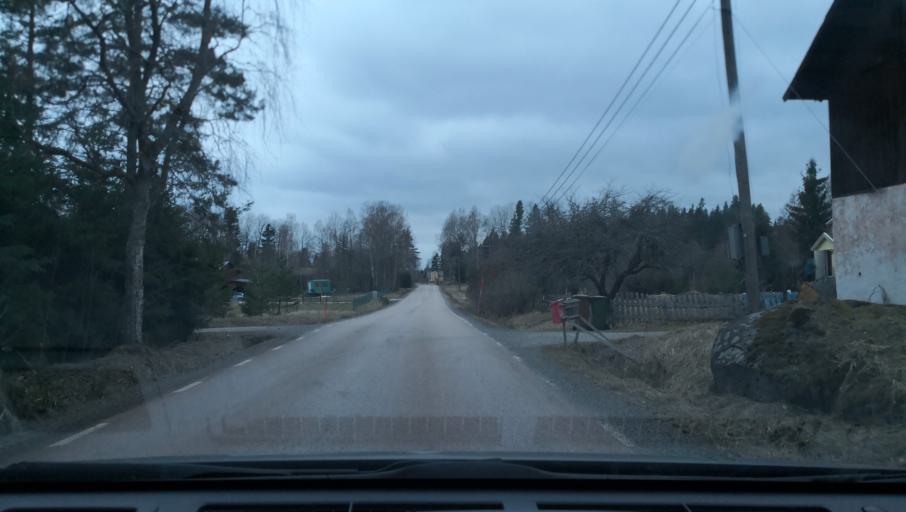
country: SE
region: Vaestmanland
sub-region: Kopings Kommun
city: Kolsva
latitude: 59.5639
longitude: 15.7528
